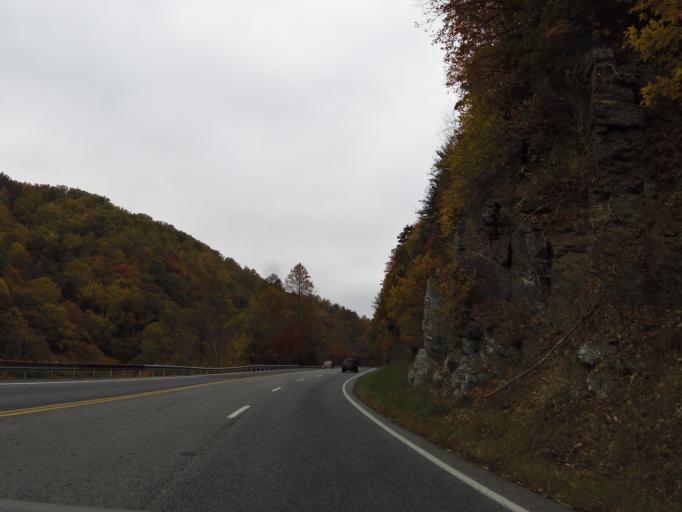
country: US
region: Virginia
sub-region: Carroll County
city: Cana
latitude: 36.6450
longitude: -80.6946
